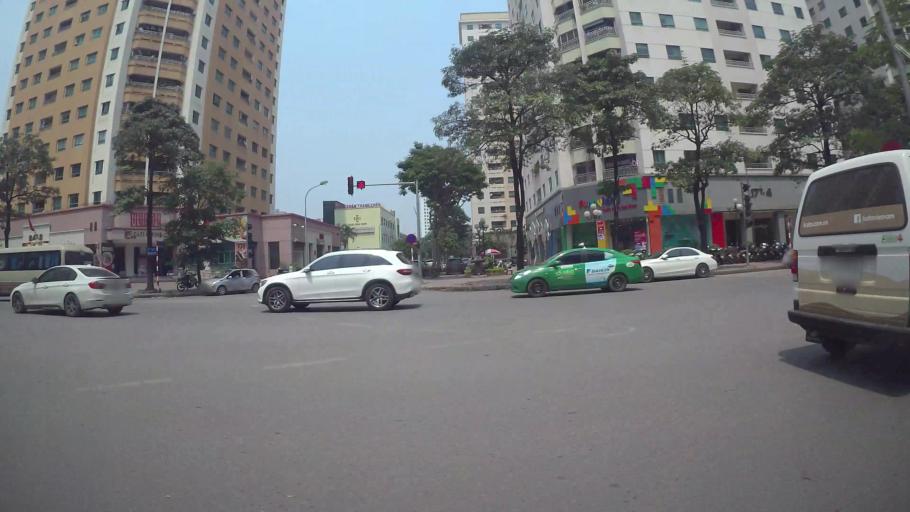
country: VN
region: Ha Noi
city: Thanh Xuan
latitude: 21.0069
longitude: 105.8030
